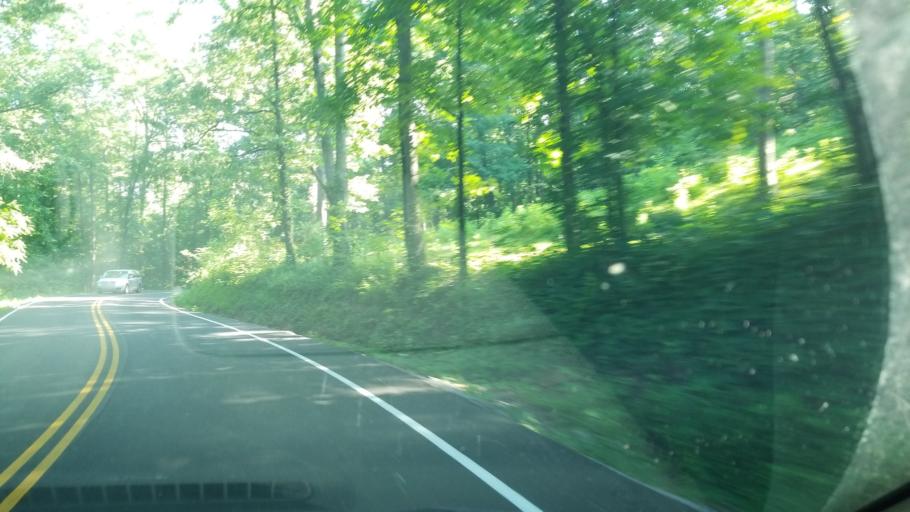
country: US
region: Tennessee
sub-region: Loudon County
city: Loudon
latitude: 35.7899
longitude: -84.3602
